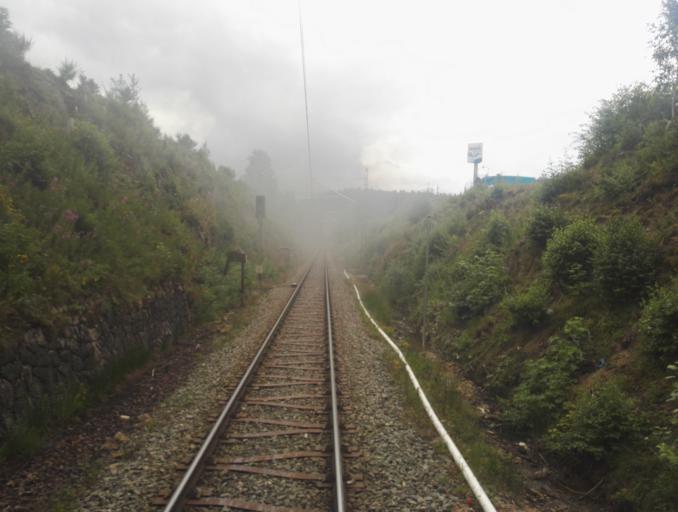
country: DE
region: Baden-Wuerttemberg
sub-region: Freiburg Region
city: Schluchsee
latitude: 47.8141
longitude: 8.1794
